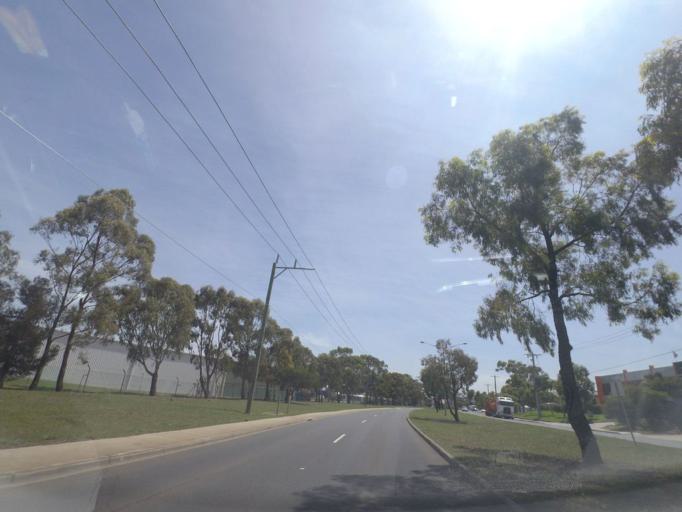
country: AU
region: Victoria
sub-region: Brimbank
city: Keilor Park
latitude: -37.7148
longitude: 144.8655
